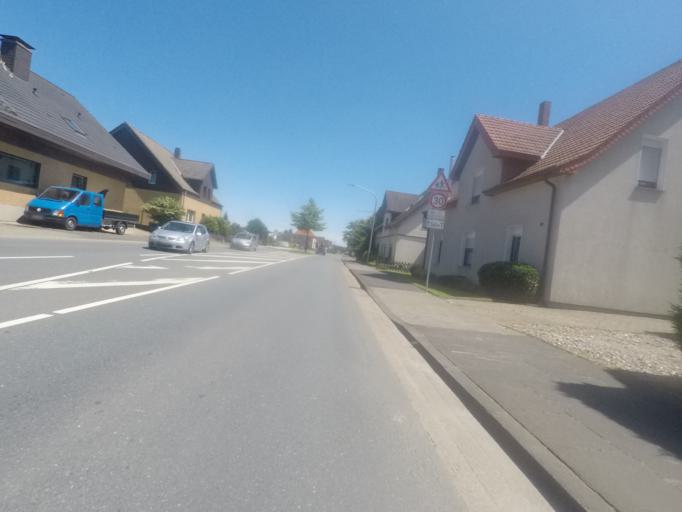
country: DE
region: North Rhine-Westphalia
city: Enger
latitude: 52.0984
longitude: 8.5345
